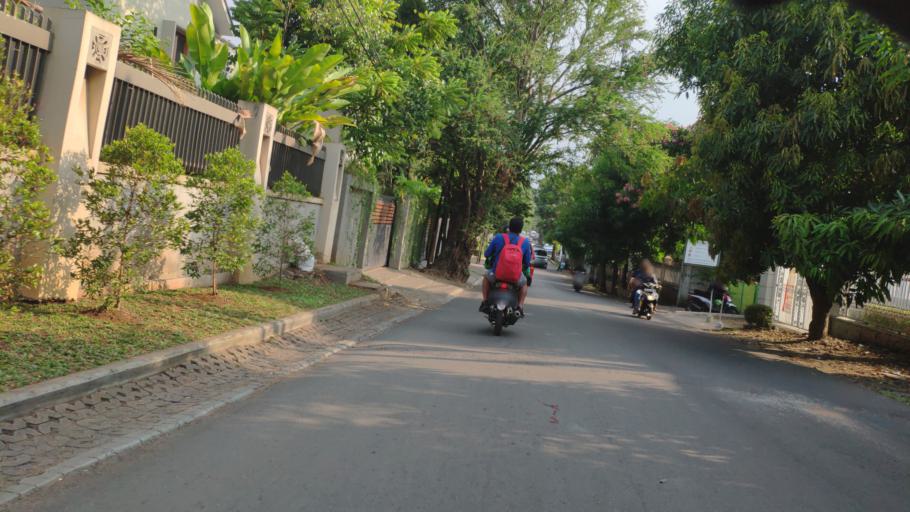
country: ID
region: Jakarta Raya
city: Jakarta
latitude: -6.2807
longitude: 106.7996
